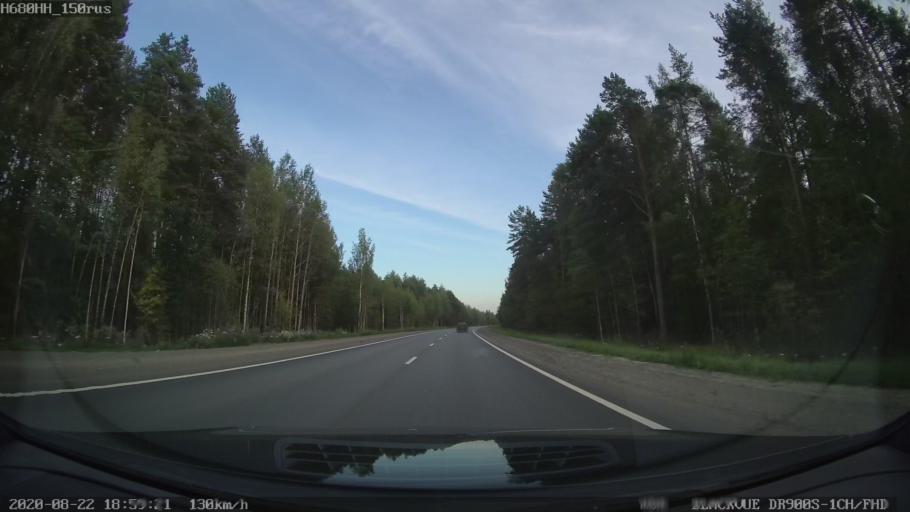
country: RU
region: Tverskaya
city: Rameshki
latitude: 57.1443
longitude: 36.0954
